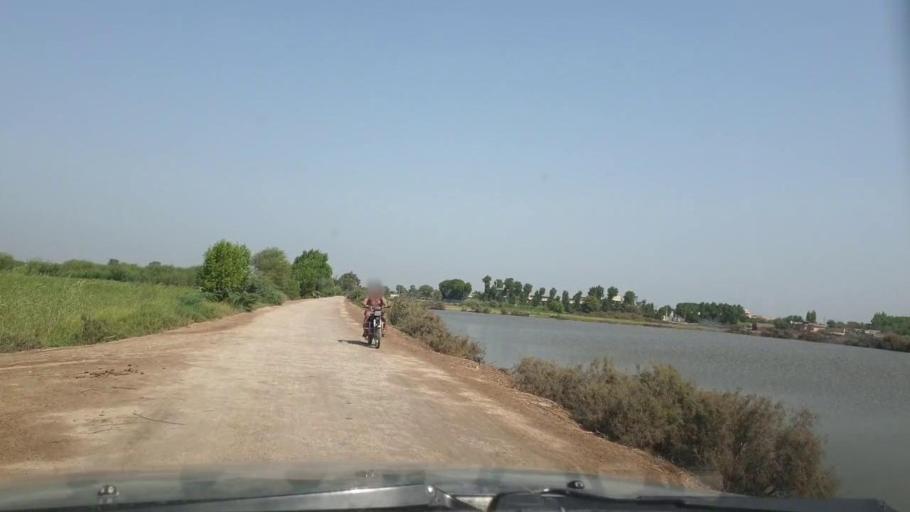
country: PK
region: Sindh
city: Tando Ghulam Ali
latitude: 25.0995
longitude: 68.7653
